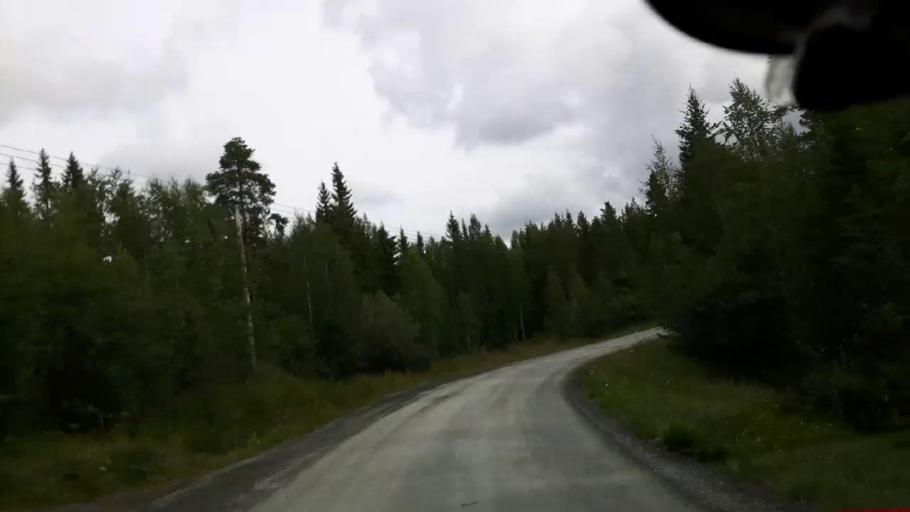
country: SE
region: Jaemtland
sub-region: Krokoms Kommun
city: Krokom
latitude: 63.5766
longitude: 14.2304
